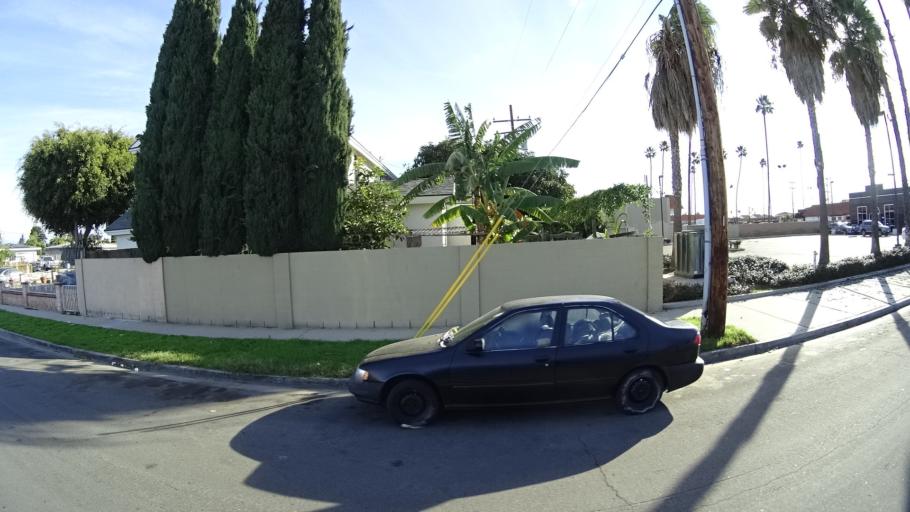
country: US
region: California
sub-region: Orange County
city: Garden Grove
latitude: 33.7607
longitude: -117.9394
